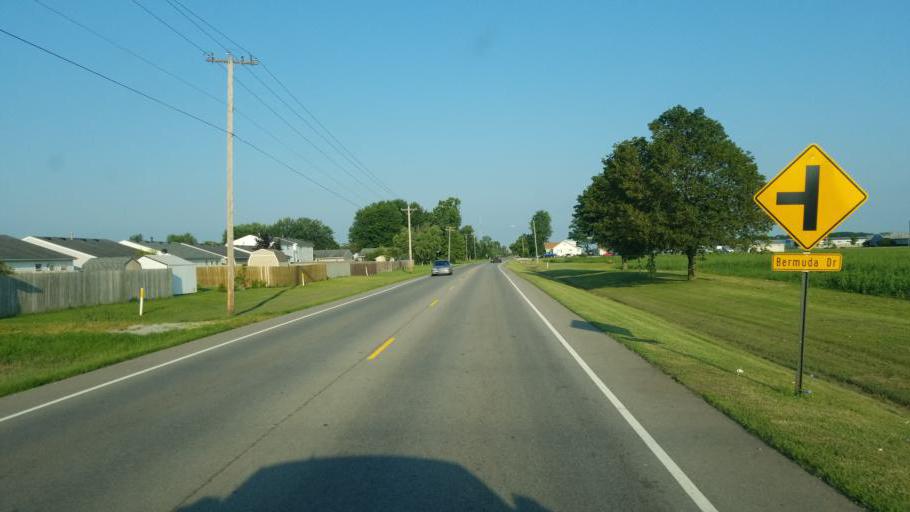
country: US
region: Ohio
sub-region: Marion County
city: Marion
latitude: 40.6150
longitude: -83.1105
